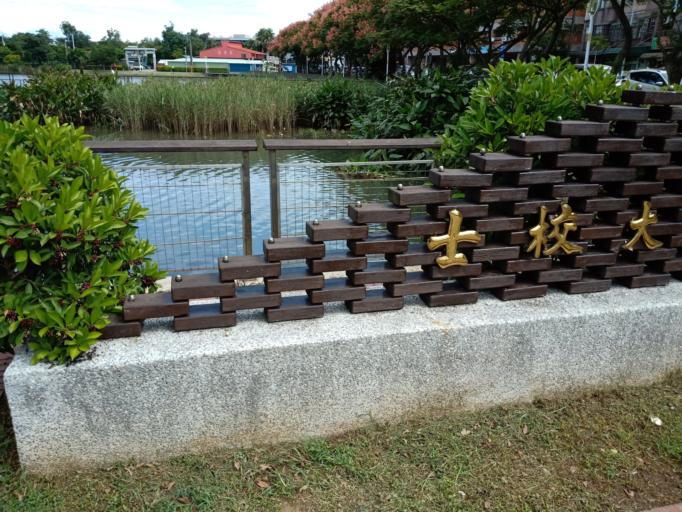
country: TW
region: Taiwan
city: Daxi
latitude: 24.9401
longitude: 121.2566
